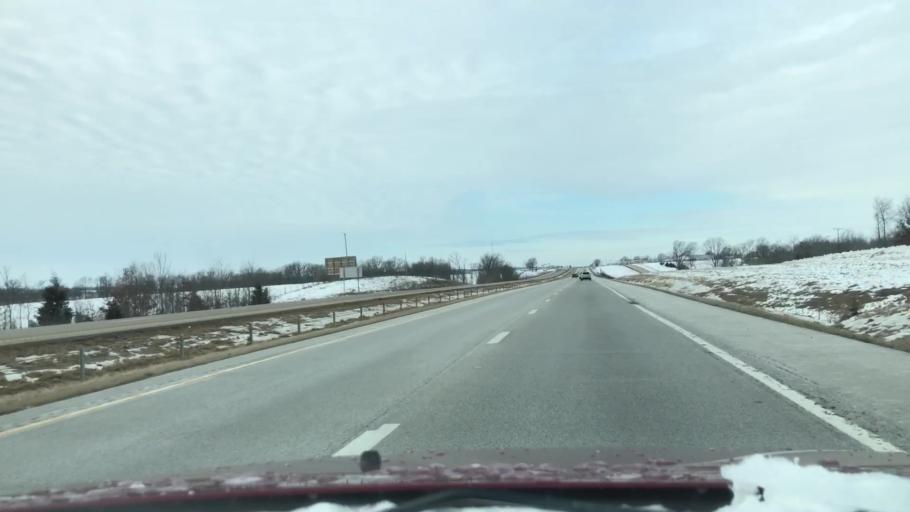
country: US
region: Missouri
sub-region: Cooper County
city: Boonville
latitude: 38.9348
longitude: -92.8260
